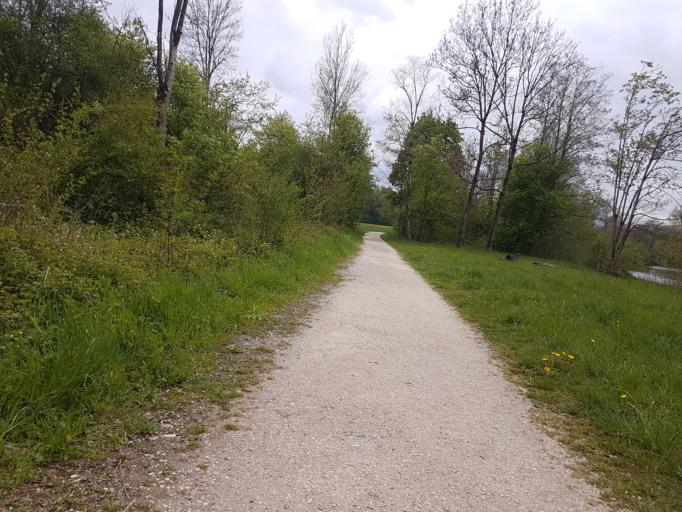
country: CH
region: Bern
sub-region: Oberaargau
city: Herzogenbuchsee
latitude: 47.2257
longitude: 7.7191
